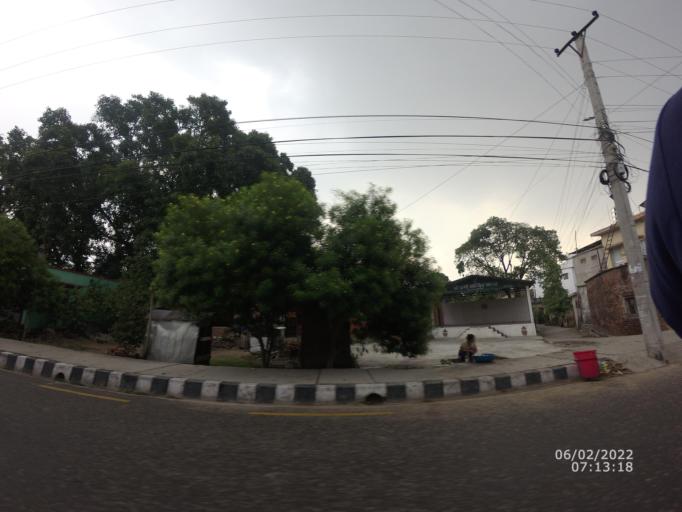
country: NP
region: Western Region
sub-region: Lumbini Zone
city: Bhairahawa
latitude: 27.4822
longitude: 83.4423
